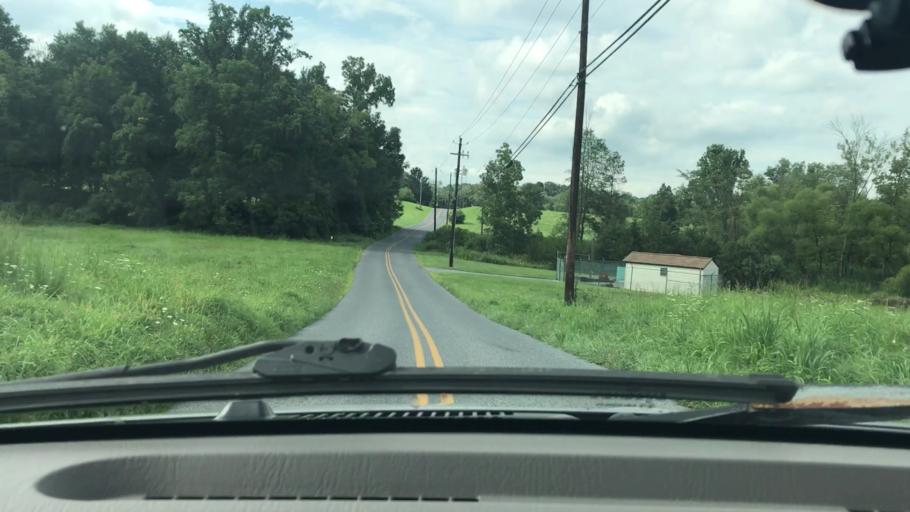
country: US
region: Pennsylvania
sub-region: Lancaster County
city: Elizabethtown
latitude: 40.1721
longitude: -76.6200
